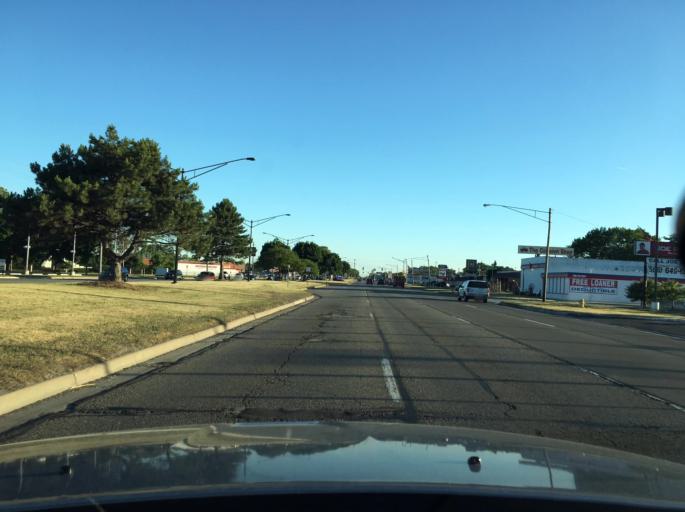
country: US
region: Michigan
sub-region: Macomb County
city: Fraser
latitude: 42.5431
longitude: -82.9070
